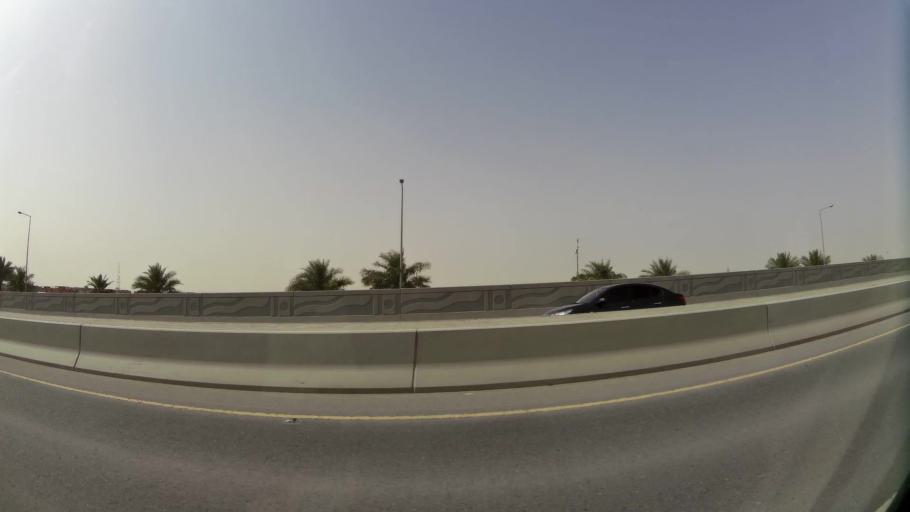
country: QA
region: Baladiyat ar Rayyan
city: Ar Rayyan
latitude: 25.2240
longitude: 51.4294
